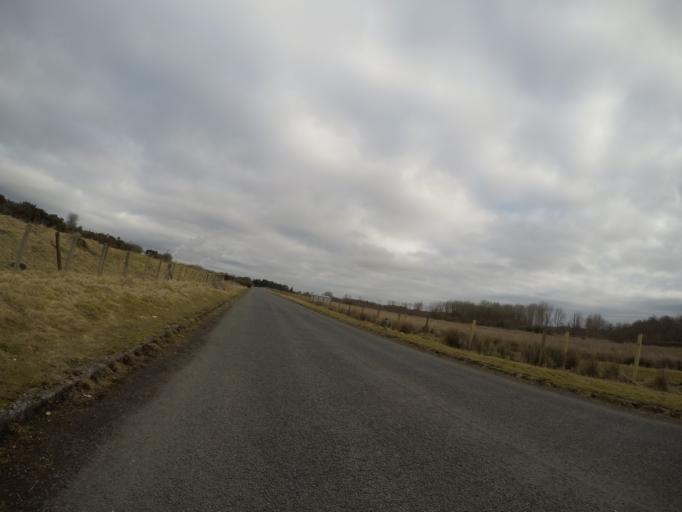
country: GB
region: Scotland
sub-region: North Ayrshire
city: Dreghorn
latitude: 55.5739
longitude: -4.6368
